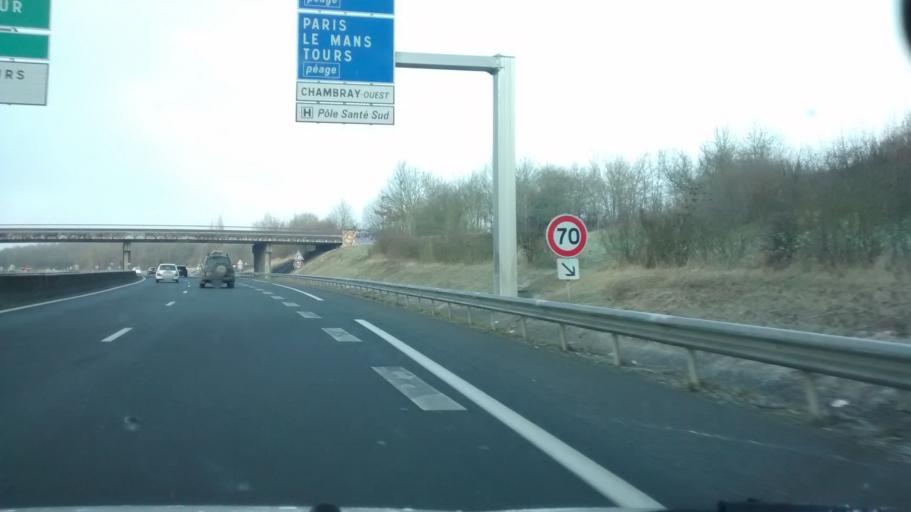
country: FR
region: Centre
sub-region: Departement d'Indre-et-Loire
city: Chambray-les-Tours
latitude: 47.3308
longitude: 0.6854
